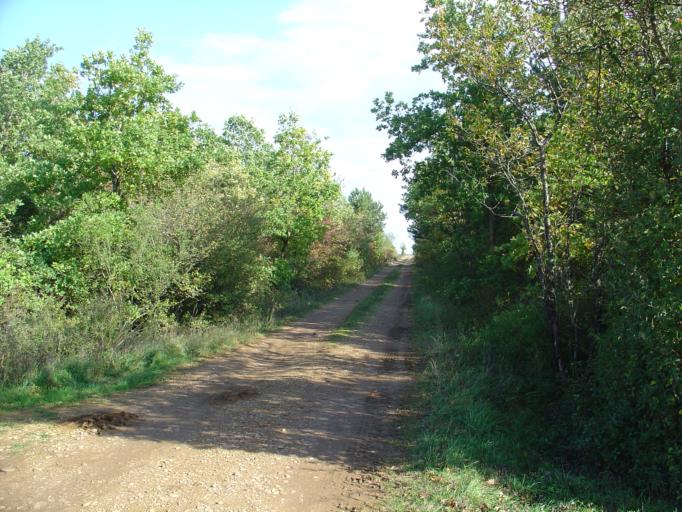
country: FR
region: Lorraine
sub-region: Departement de Meurthe-et-Moselle
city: Colombey-les-Belles
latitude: 48.5414
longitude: 5.8901
